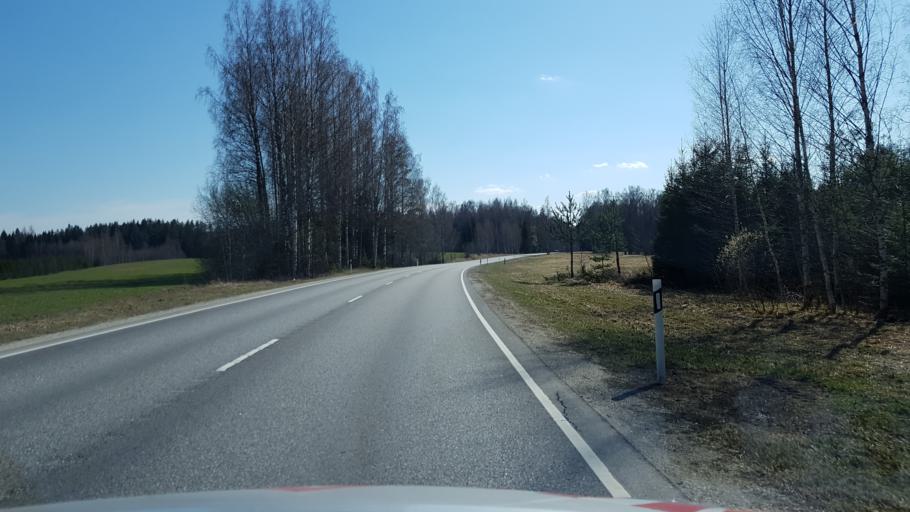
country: EE
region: Jogevamaa
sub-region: Mustvee linn
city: Mustvee
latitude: 58.6993
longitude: 26.8173
